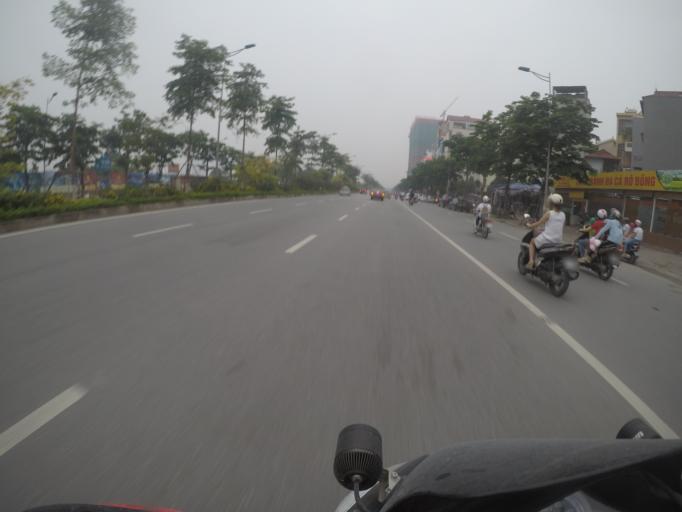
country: VN
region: Ha Noi
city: Tay Ho
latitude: 21.0519
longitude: 105.8045
